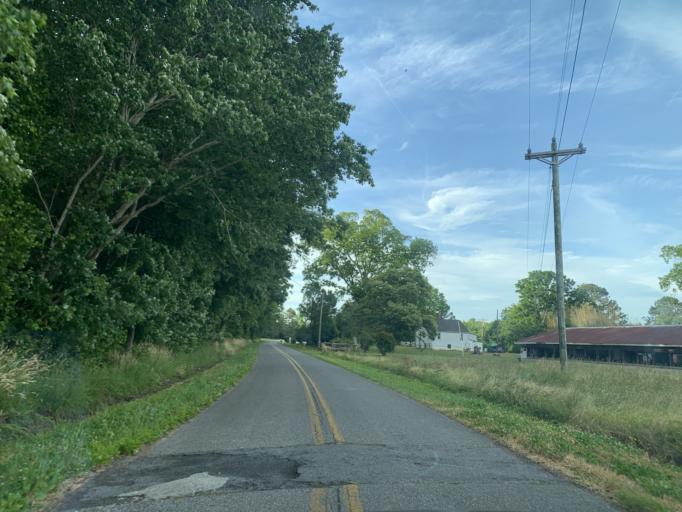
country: US
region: Maryland
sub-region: Worcester County
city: Pocomoke City
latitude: 38.0764
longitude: -75.4778
